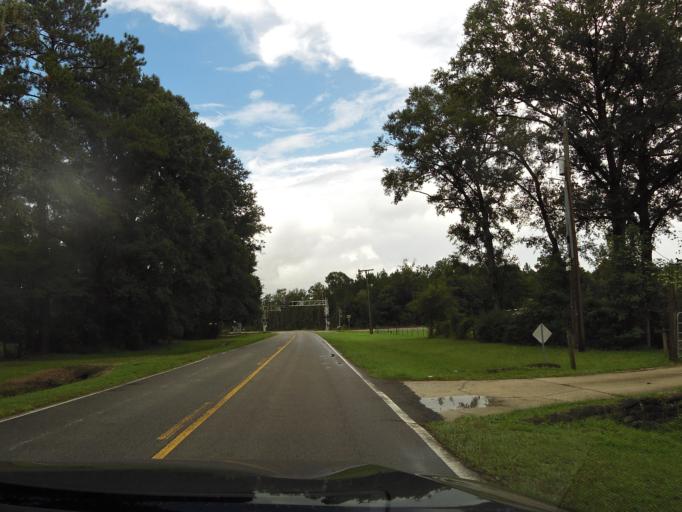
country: US
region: Florida
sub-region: Duval County
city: Baldwin
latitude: 30.3922
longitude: -81.9411
